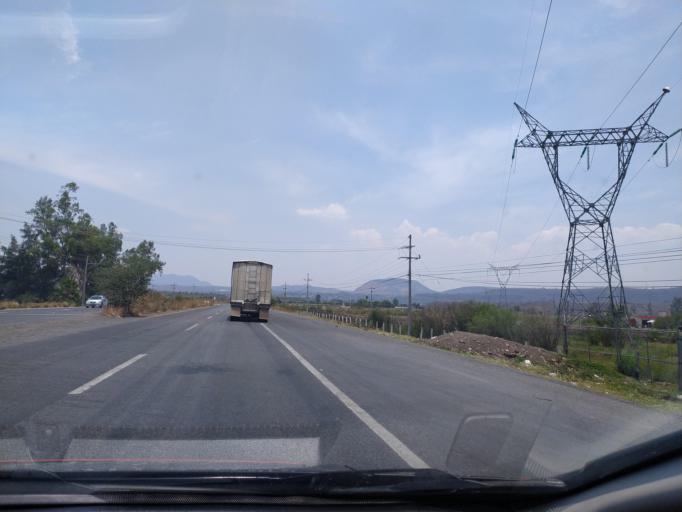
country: MX
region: Jalisco
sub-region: Acatlan de Juarez
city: Villa de los Ninos
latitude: 20.3931
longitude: -103.5933
